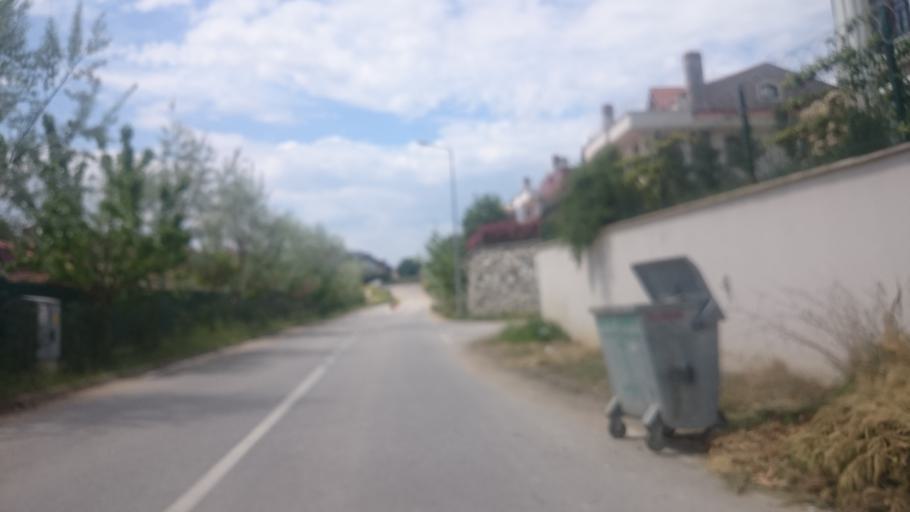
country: TR
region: Bursa
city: Gorukle
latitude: 40.2294
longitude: 28.8944
